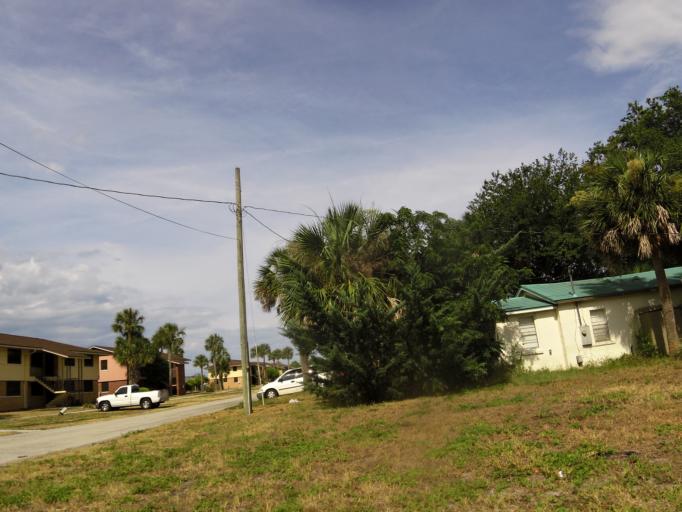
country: US
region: Florida
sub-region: Duval County
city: Jacksonville Beach
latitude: 30.2859
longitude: -81.3993
